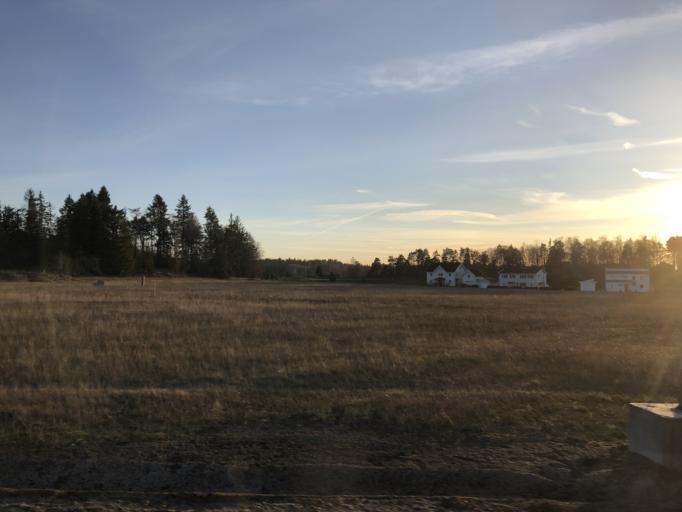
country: SE
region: Stockholm
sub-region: Jarfalla Kommun
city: Jakobsberg
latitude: 59.4128
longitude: 17.8813
